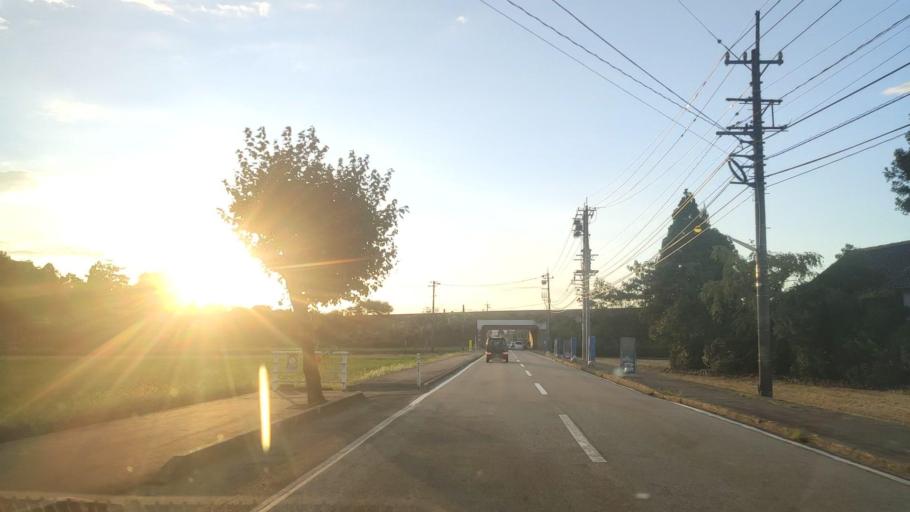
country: JP
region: Toyama
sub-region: Oyabe Shi
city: Oyabe
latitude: 36.6276
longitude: 136.8821
